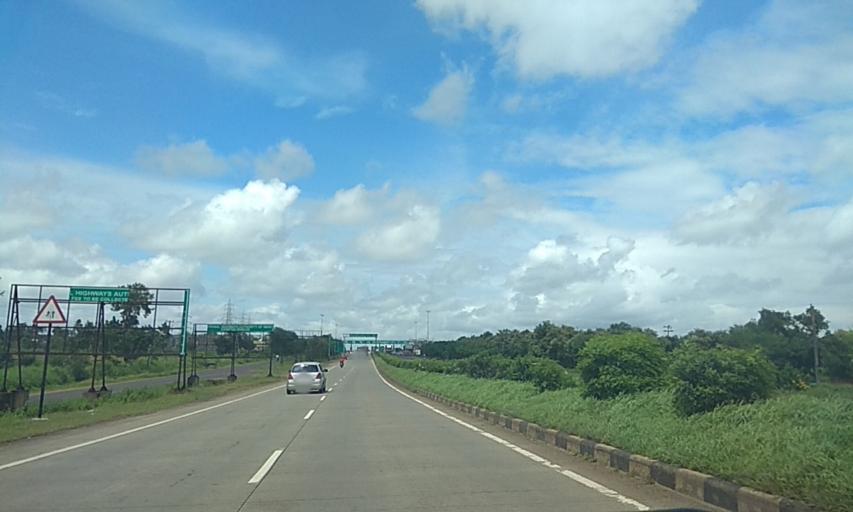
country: IN
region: Karnataka
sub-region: Belgaum
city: Sankeshwar
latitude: 16.1388
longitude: 74.5167
